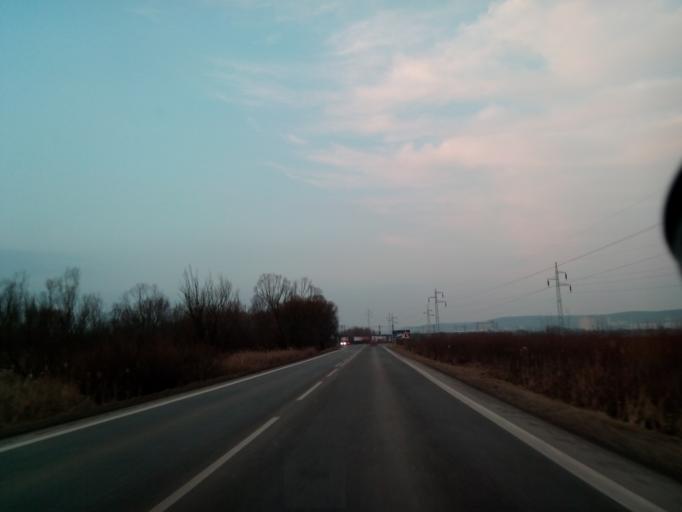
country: SK
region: Kosicky
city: Kosice
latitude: 48.6630
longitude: 21.2717
